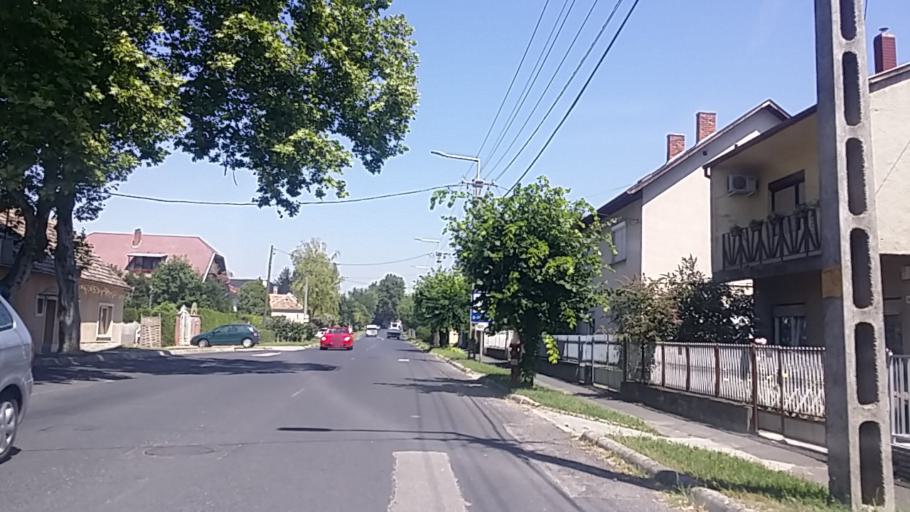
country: HU
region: Zala
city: Keszthely
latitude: 46.7728
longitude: 17.2386
